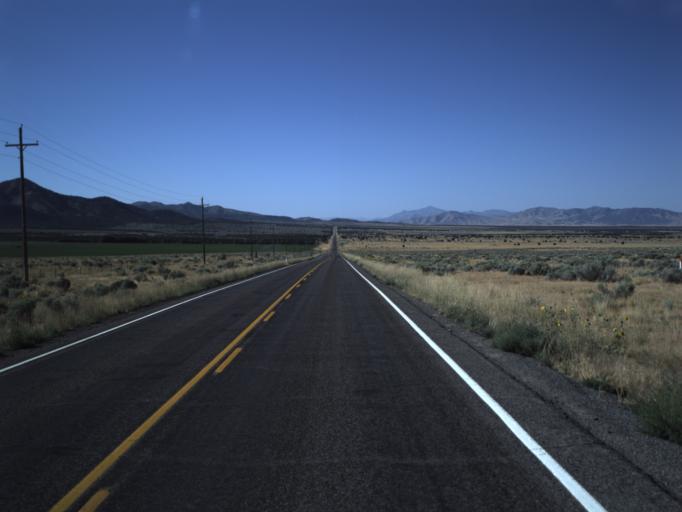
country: US
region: Utah
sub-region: Juab County
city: Mona
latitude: 39.8967
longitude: -112.1380
